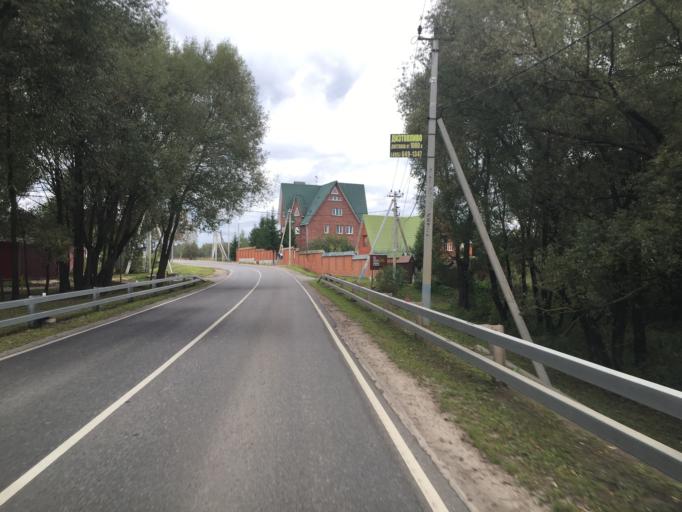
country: RU
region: Moskovskaya
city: Vatutinki
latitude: 55.4895
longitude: 37.4019
